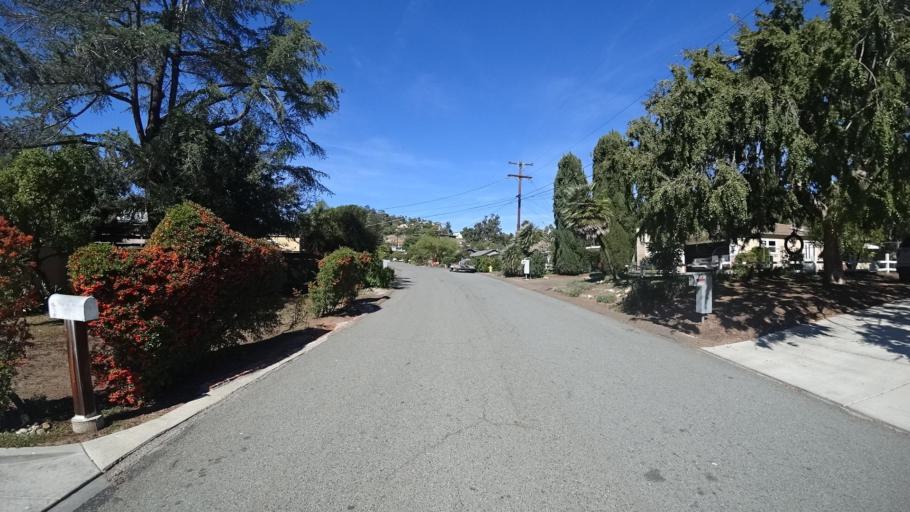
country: US
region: California
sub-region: San Diego County
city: Casa de Oro-Mount Helix
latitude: 32.7536
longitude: -116.9686
